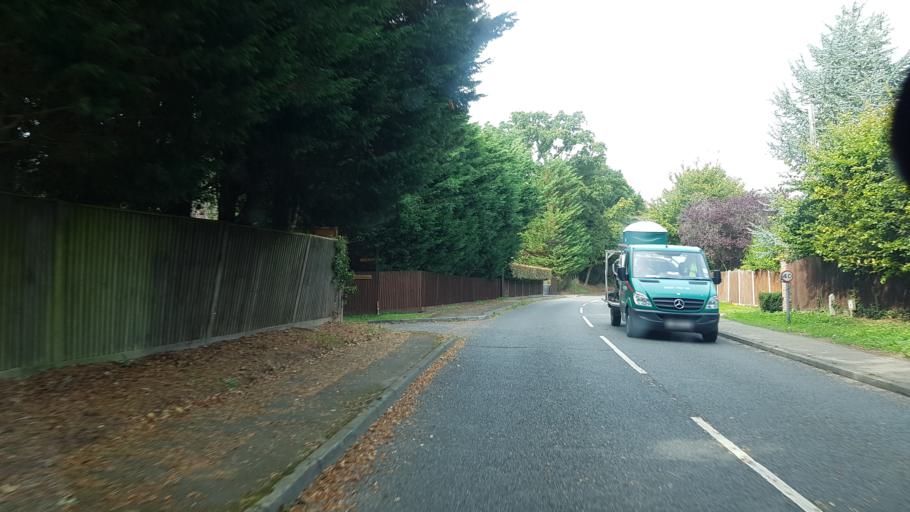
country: GB
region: England
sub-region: Kent
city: West Malling
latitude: 51.3051
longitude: 0.3762
